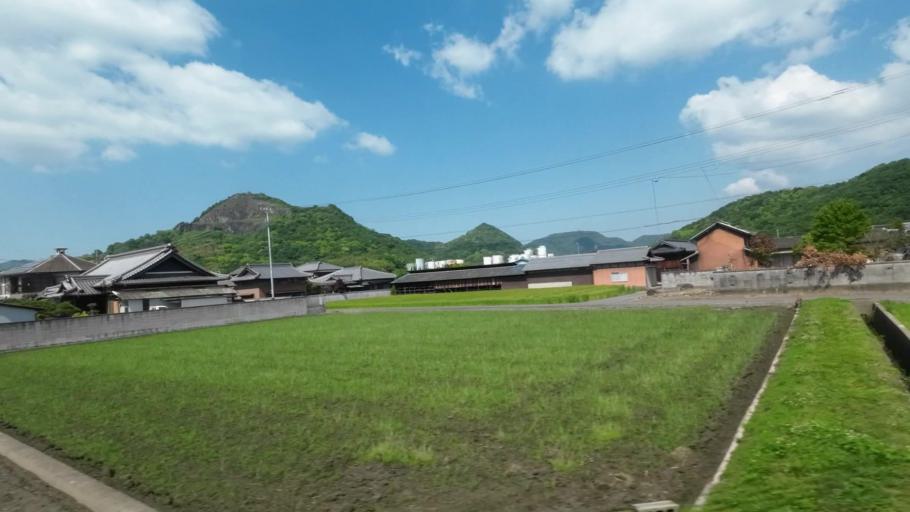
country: JP
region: Kagawa
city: Kan'onjicho
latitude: 34.1904
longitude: 133.7130
